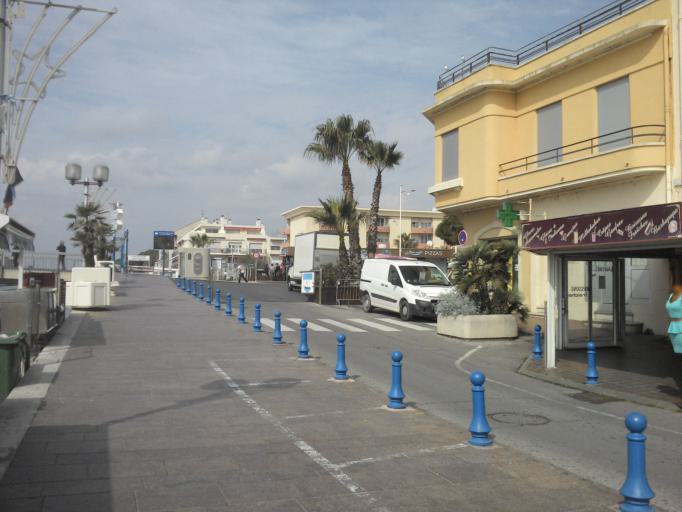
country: FR
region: Languedoc-Roussillon
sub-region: Departement de l'Herault
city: Palavas-les-Flots
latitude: 43.5286
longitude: 3.9296
